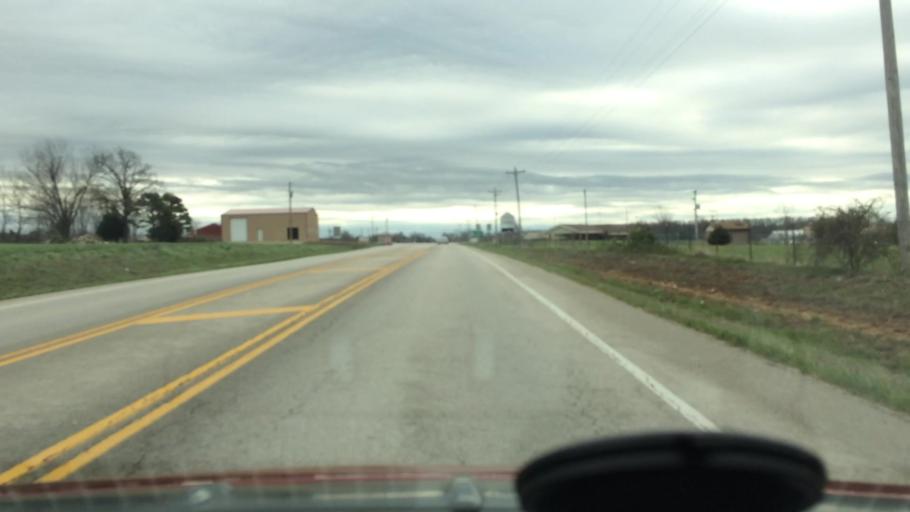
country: US
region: Missouri
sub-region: Webster County
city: Marshfield
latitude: 37.3402
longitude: -92.9444
